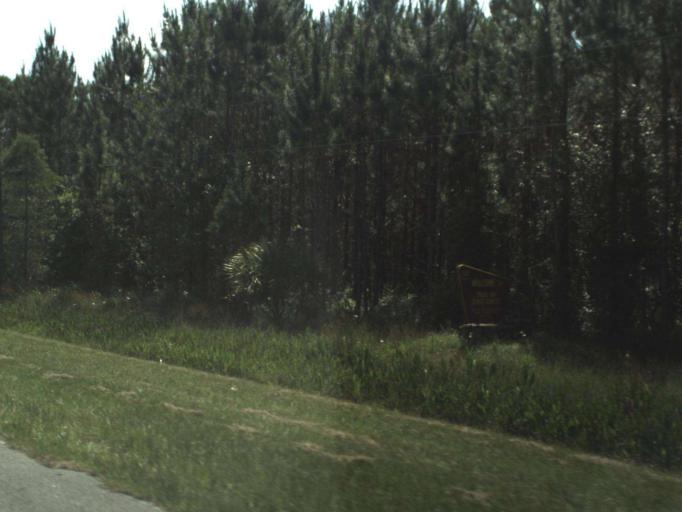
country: US
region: Florida
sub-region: Volusia County
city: North DeLand
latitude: 29.1124
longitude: -81.1925
